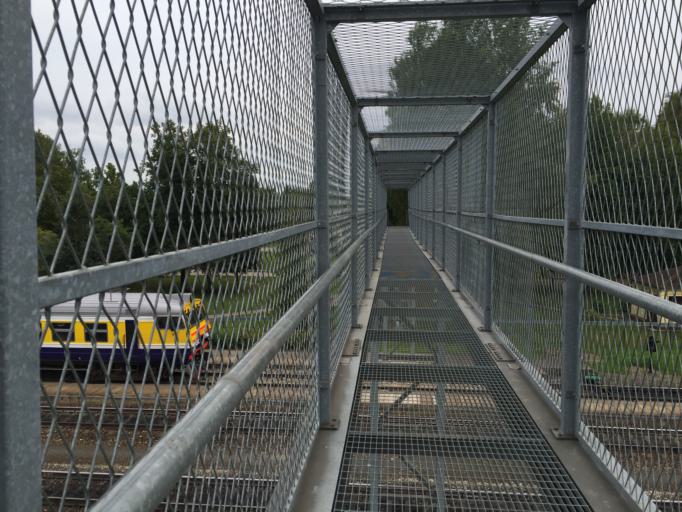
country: LV
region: Zilupes
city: Zilupe
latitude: 56.3919
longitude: 28.1164
